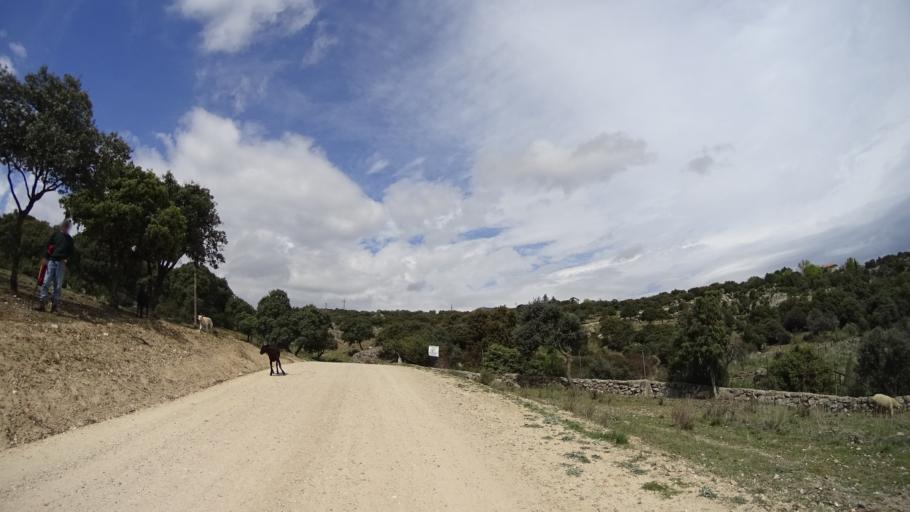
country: ES
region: Madrid
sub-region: Provincia de Madrid
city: Hoyo de Manzanares
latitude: 40.6197
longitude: -3.8827
